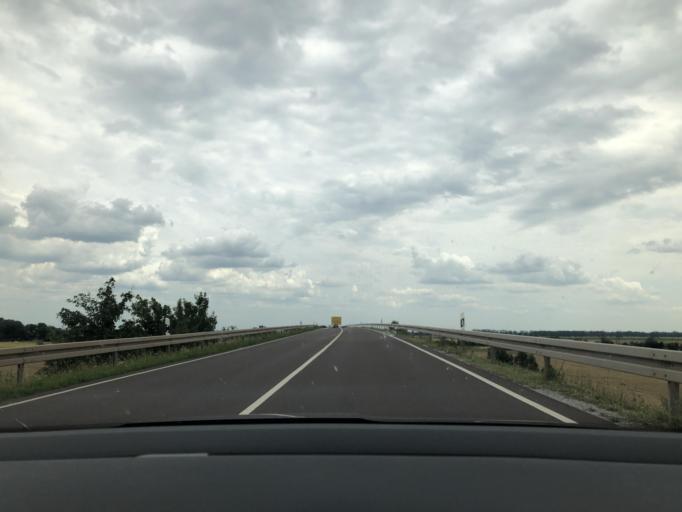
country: DE
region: Saxony-Anhalt
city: Eggersdorf
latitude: 51.9866
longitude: 11.7015
